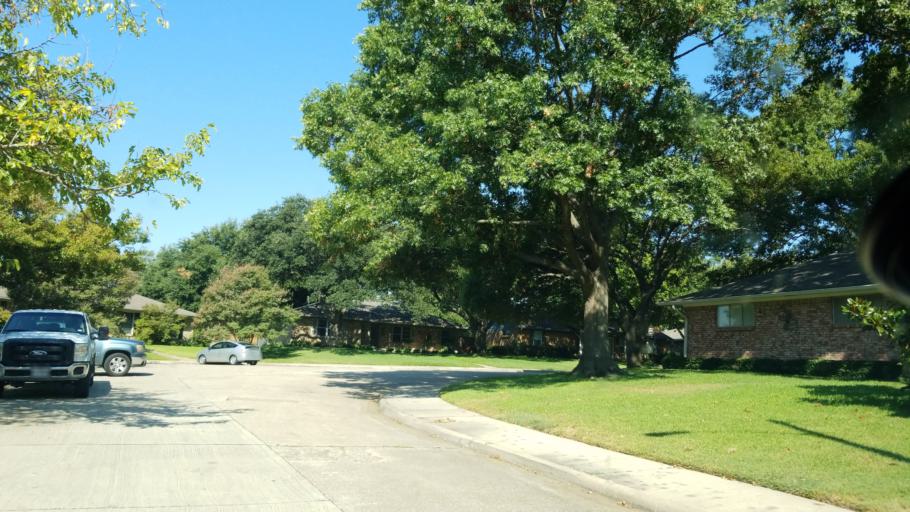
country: US
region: Texas
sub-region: Dallas County
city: Richardson
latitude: 32.9053
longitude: -96.7367
